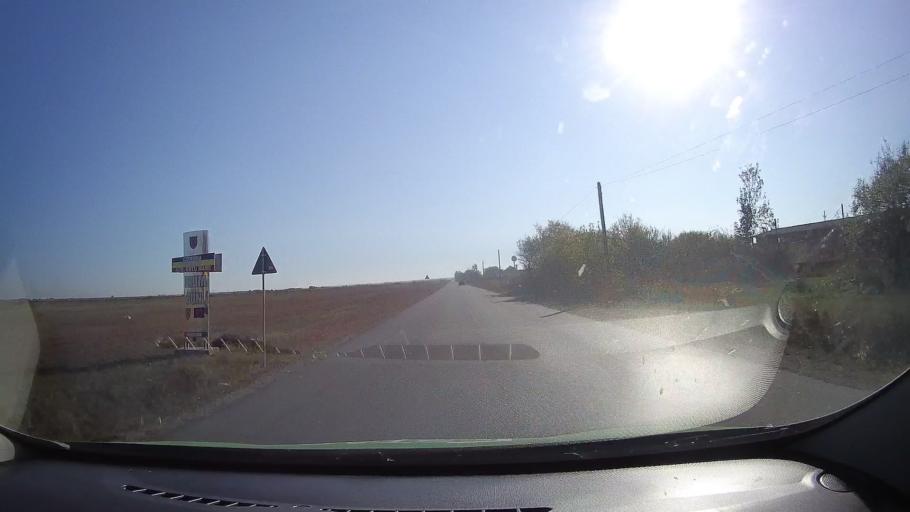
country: RO
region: Satu Mare
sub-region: Comuna Santau
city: Santau
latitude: 47.5086
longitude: 22.5212
